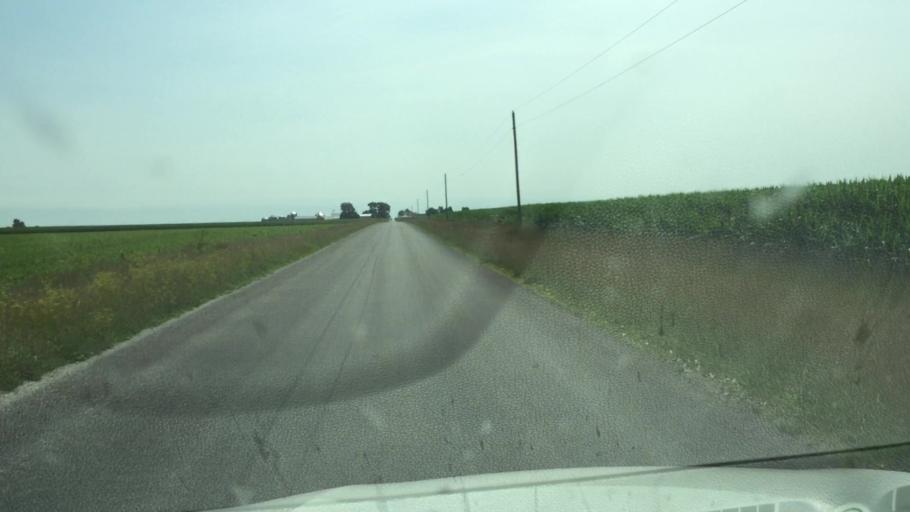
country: US
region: Illinois
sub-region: Hancock County
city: Nauvoo
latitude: 40.5074
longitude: -91.3257
